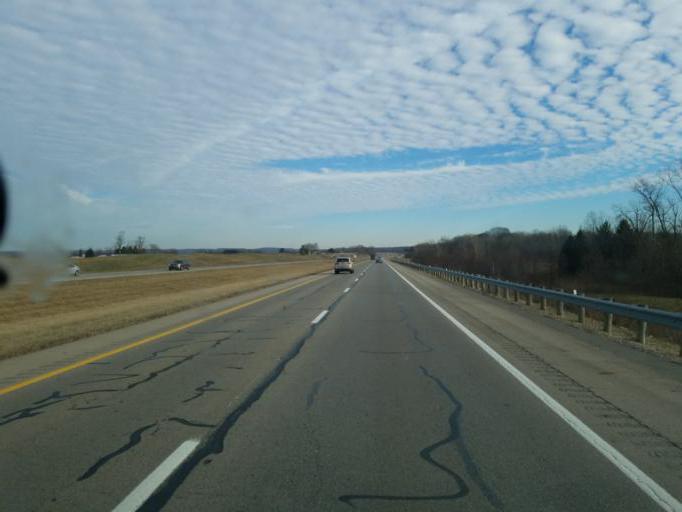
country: US
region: Ohio
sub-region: Licking County
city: Beechwood Trails
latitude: 40.0759
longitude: -82.6489
